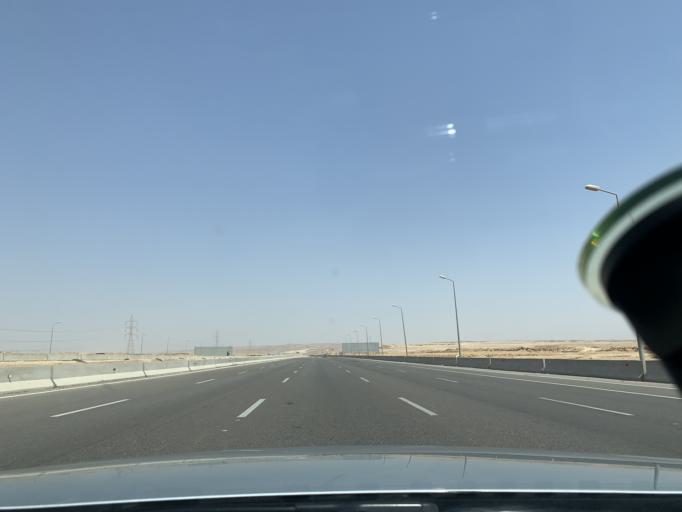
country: EG
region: As Suways
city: Ain Sukhna
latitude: 29.7648
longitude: 31.9539
